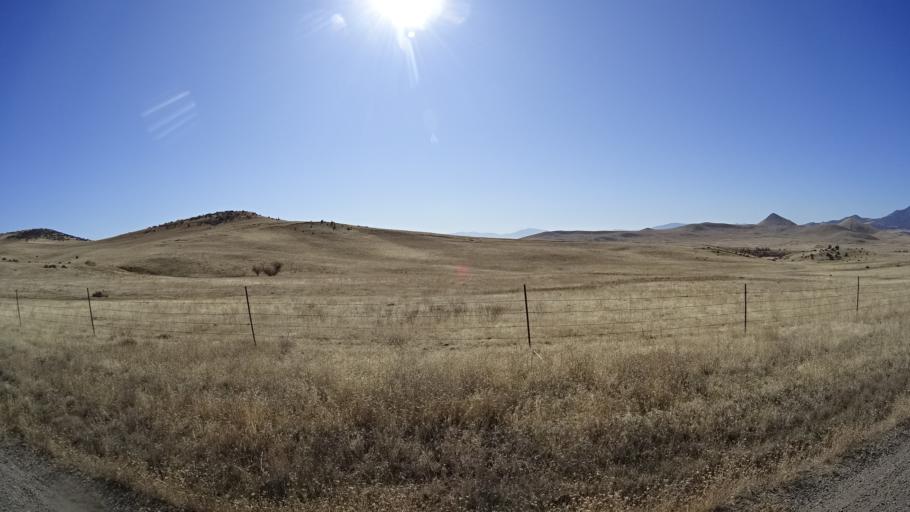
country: US
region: California
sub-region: Siskiyou County
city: Montague
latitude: 41.8469
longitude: -122.4372
